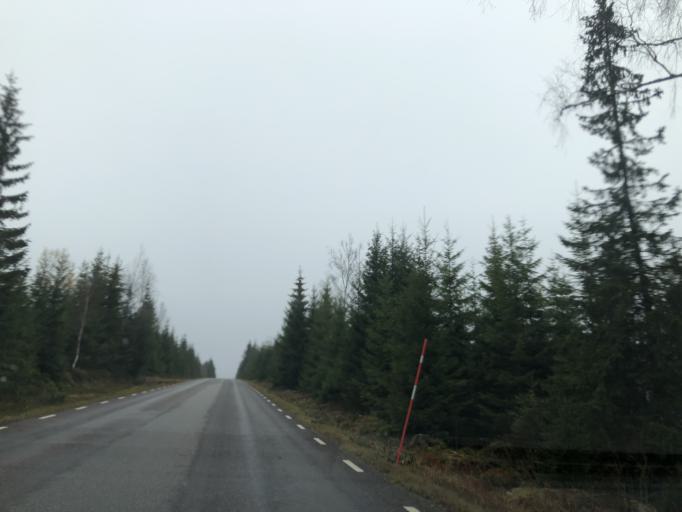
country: SE
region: Vaestra Goetaland
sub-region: Ulricehamns Kommun
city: Ulricehamn
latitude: 57.7346
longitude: 13.5428
